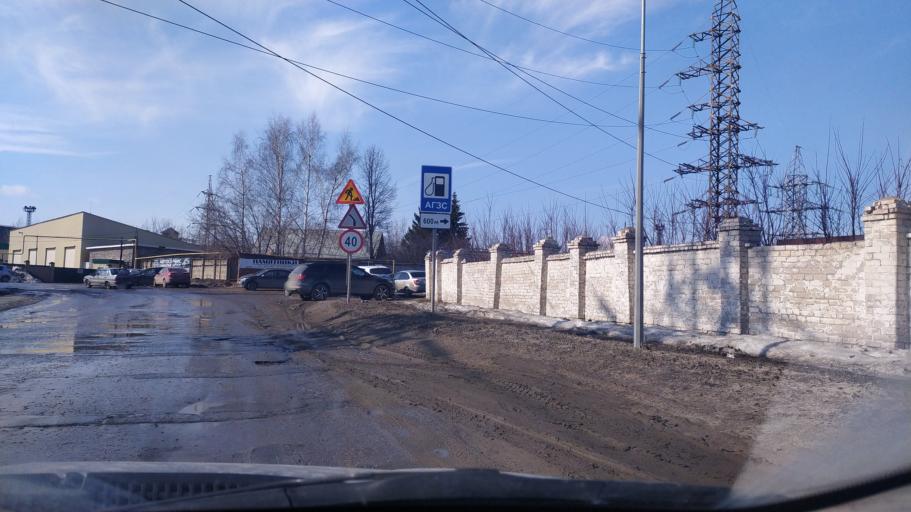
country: RU
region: Chuvashia
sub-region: Cheboksarskiy Rayon
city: Cheboksary
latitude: 56.1197
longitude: 47.2918
